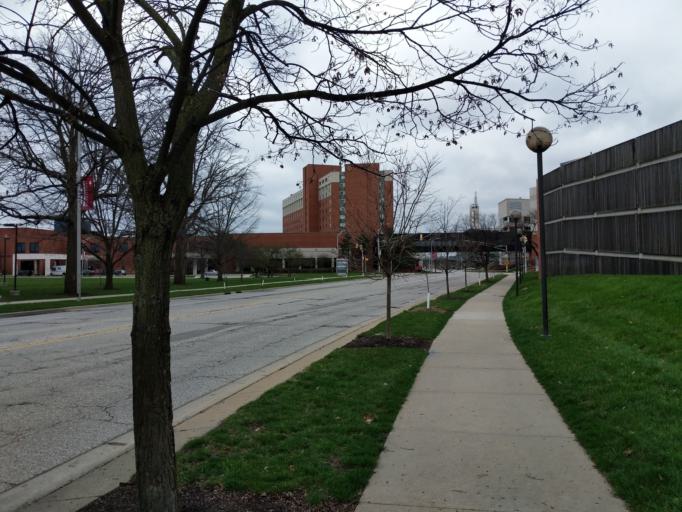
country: US
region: Indiana
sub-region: Marion County
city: Indianapolis
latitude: 39.7772
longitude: -86.1752
